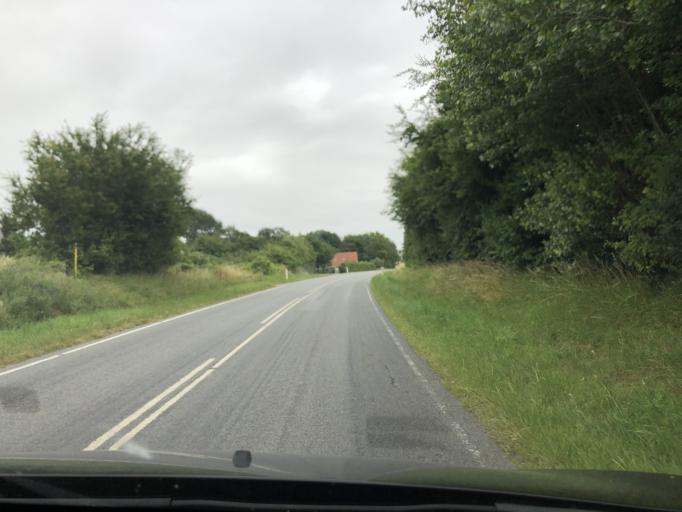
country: DK
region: South Denmark
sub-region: AEro Kommune
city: AEroskobing
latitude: 54.9258
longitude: 10.2718
